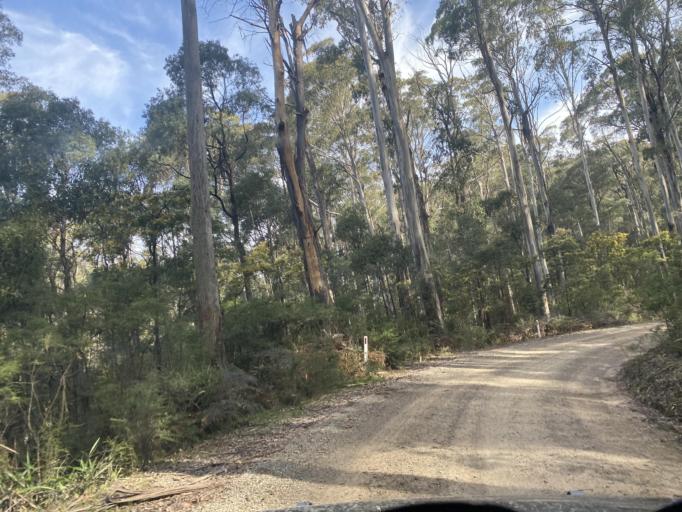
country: AU
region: Victoria
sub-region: Mansfield
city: Mansfield
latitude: -36.8548
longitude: 146.1923
